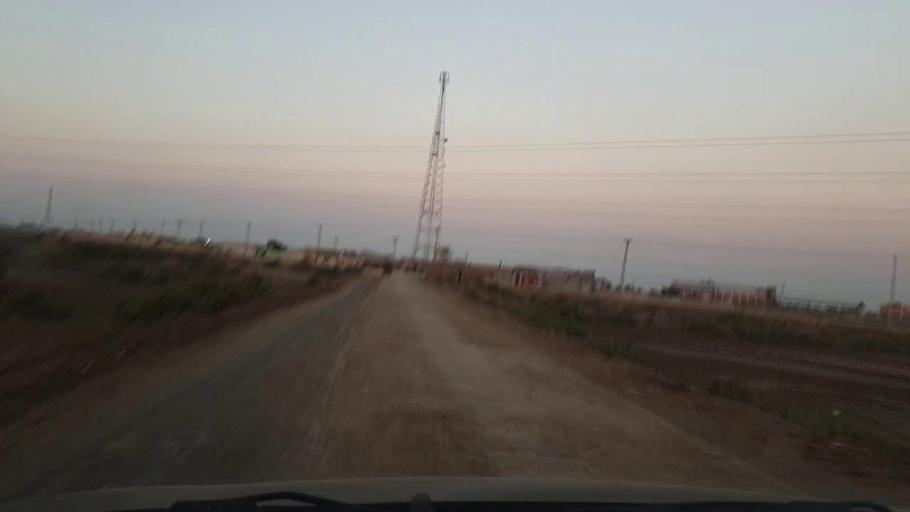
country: PK
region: Sindh
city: Jhol
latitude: 25.9515
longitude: 68.9764
